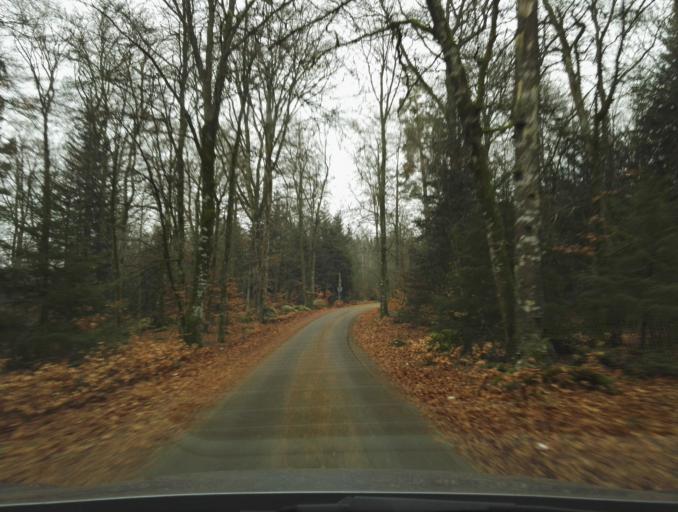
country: SE
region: Kronoberg
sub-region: Vaxjo Kommun
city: Vaexjoe
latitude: 56.9543
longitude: 14.7979
